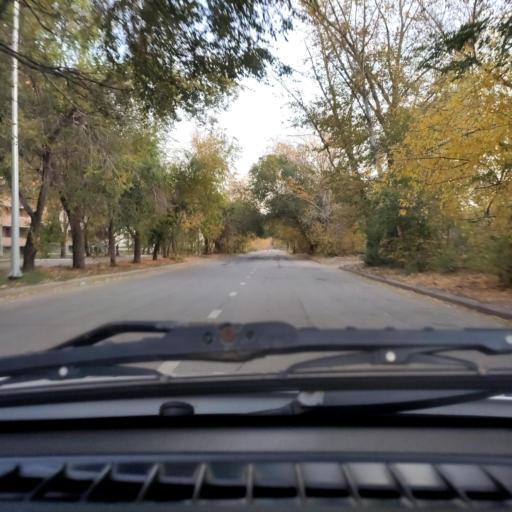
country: RU
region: Samara
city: Tol'yatti
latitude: 53.5231
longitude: 49.4314
